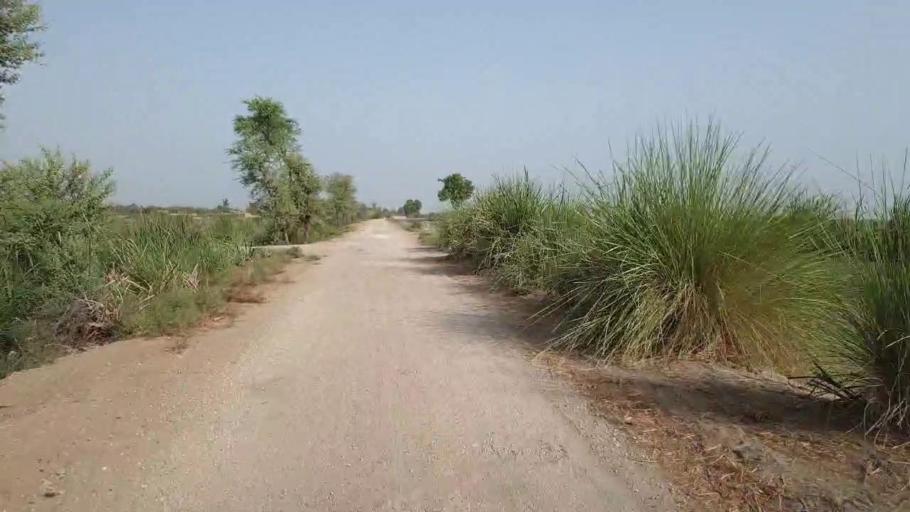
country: PK
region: Sindh
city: Daur
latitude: 26.3335
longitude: 68.1881
